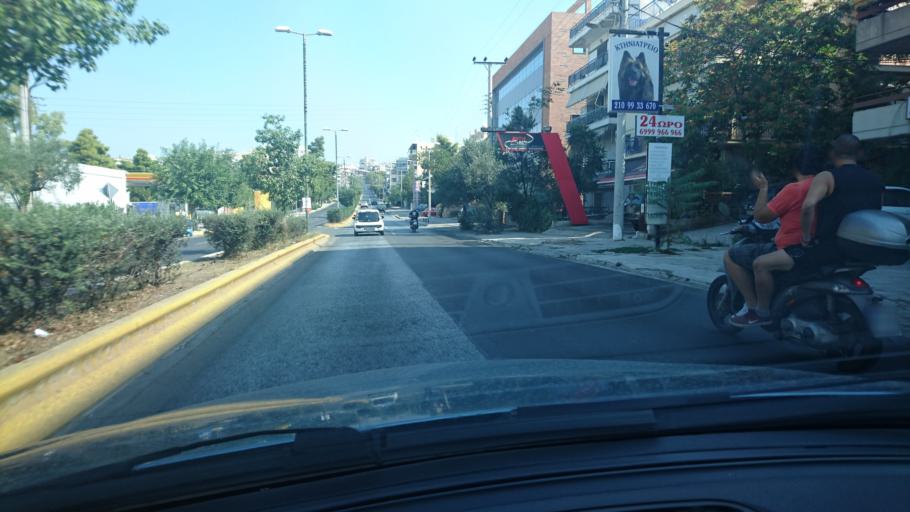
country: GR
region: Attica
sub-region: Nomarchia Athinas
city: Ilioupoli
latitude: 37.9387
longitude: 23.7602
